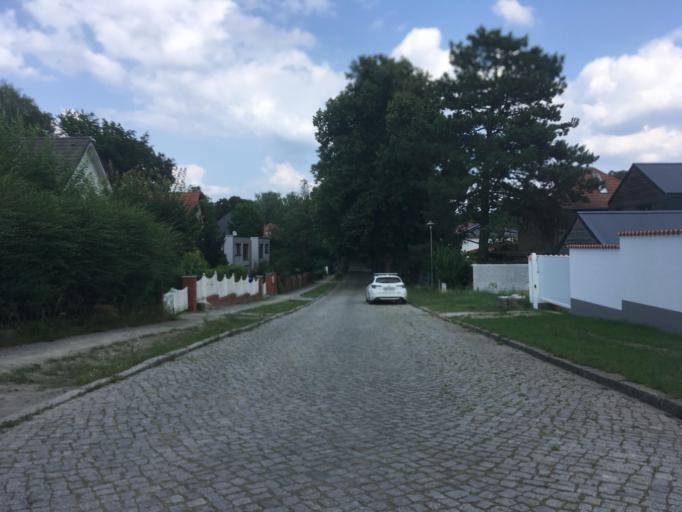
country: DE
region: Brandenburg
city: Wildau
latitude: 52.3410
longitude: 13.6263
